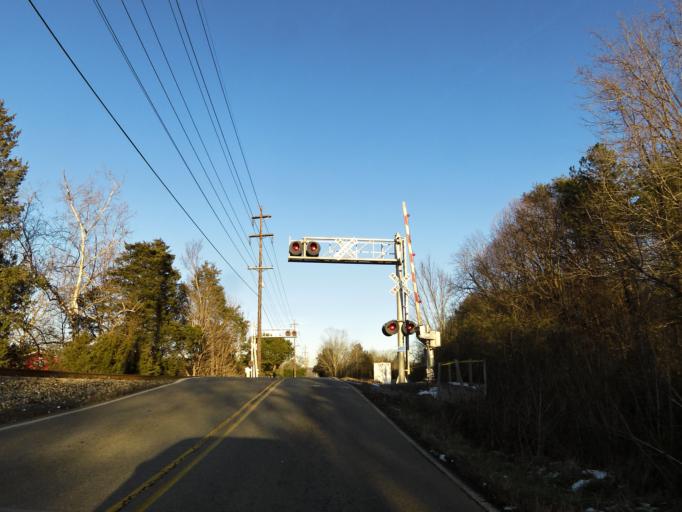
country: US
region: Tennessee
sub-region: Knox County
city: Farragut
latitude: 35.9706
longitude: -84.0720
